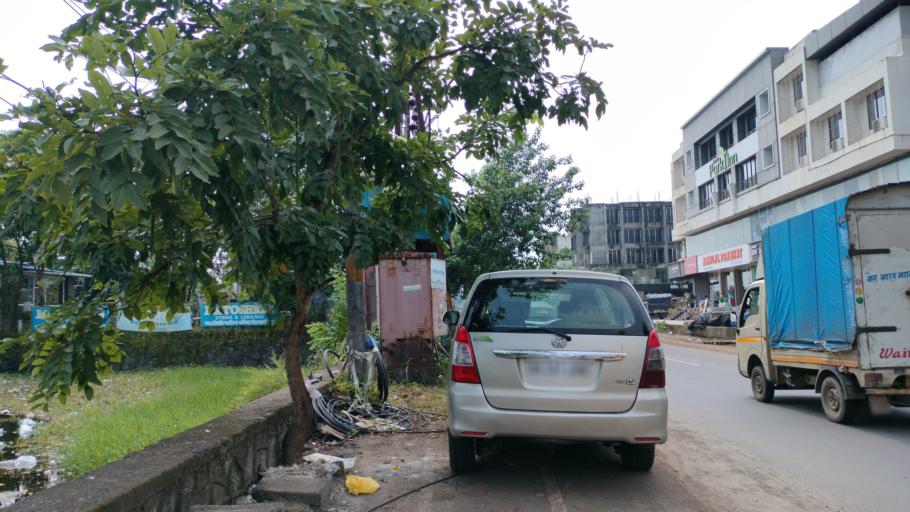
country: IN
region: Maharashtra
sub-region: Thane
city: Bhayandar
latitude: 19.3654
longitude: 72.8117
